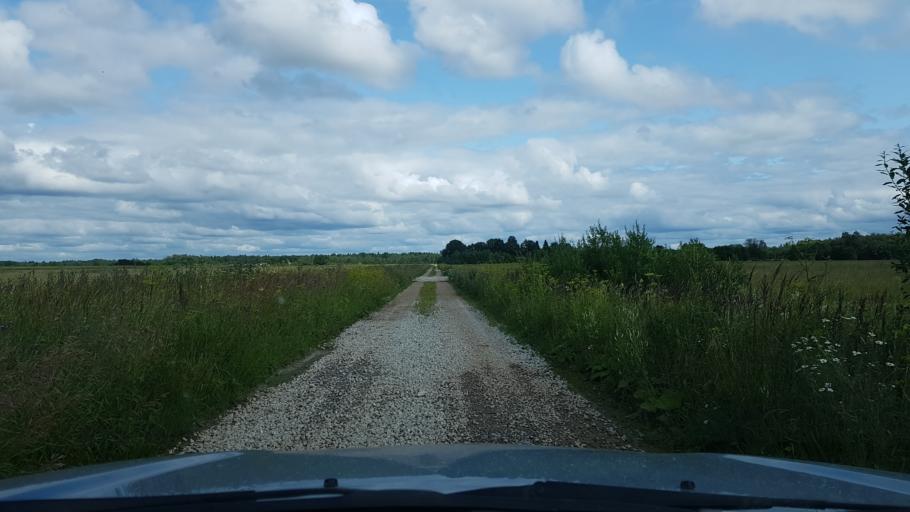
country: EE
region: Ida-Virumaa
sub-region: Narva-Joesuu linn
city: Narva-Joesuu
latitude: 59.3701
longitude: 27.9376
